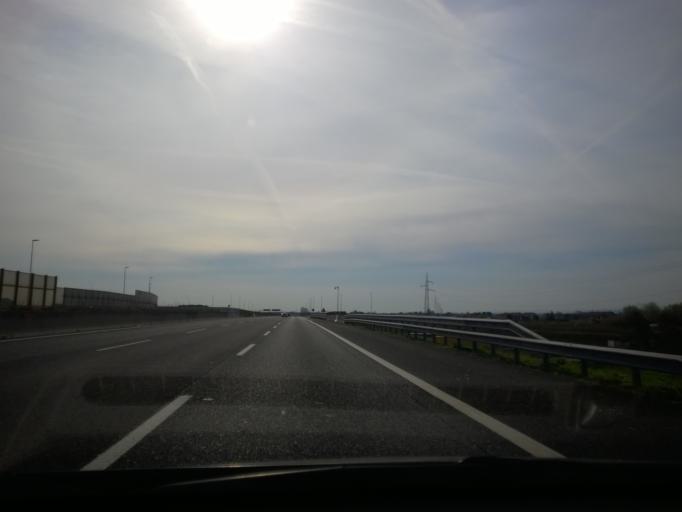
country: IT
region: Emilia-Romagna
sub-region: Forli-Cesena
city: Cesena
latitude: 44.1691
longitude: 12.2854
